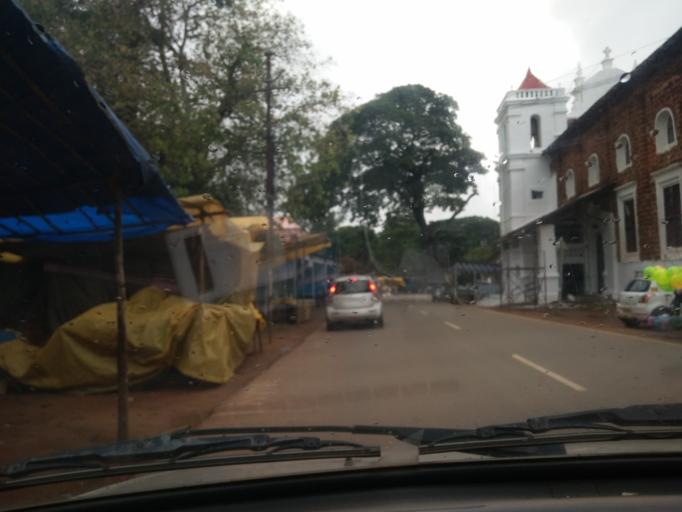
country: IN
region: Goa
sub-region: South Goa
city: Colva
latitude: 15.2785
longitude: 73.9231
